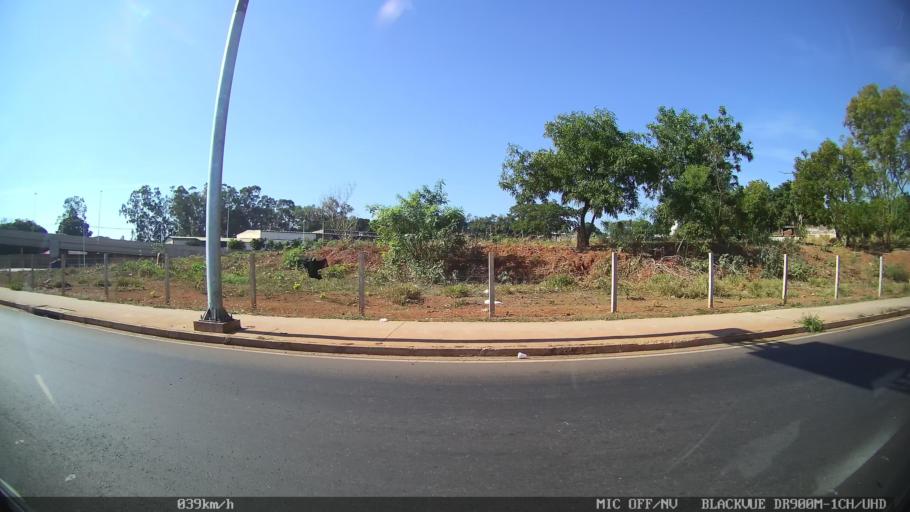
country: BR
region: Sao Paulo
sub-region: Sao Jose Do Rio Preto
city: Sao Jose do Rio Preto
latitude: -20.7903
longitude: -49.3896
